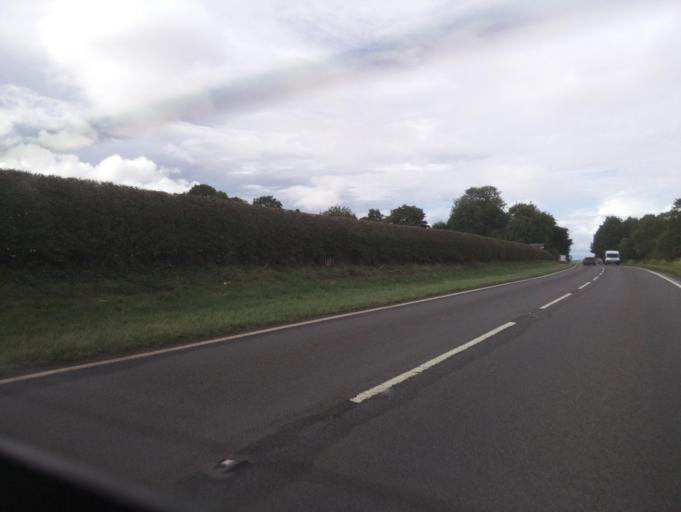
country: GB
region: England
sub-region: Telford and Wrekin
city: Madeley
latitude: 52.5923
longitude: -2.3986
